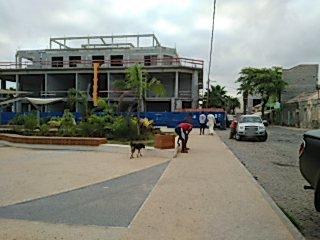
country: CV
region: Sal
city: Santa Maria
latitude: 16.5984
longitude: -22.9055
